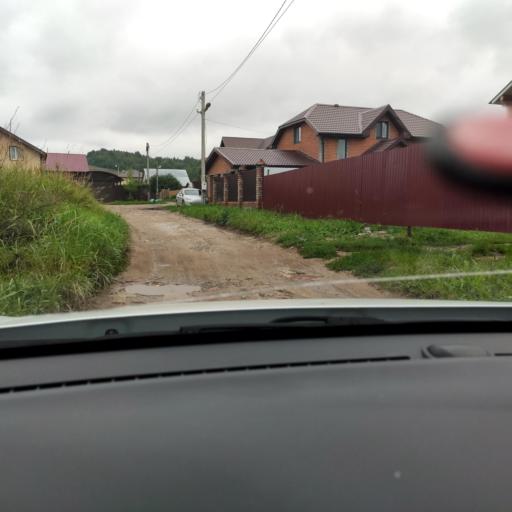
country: RU
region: Tatarstan
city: Stolbishchi
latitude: 55.7469
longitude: 49.3101
